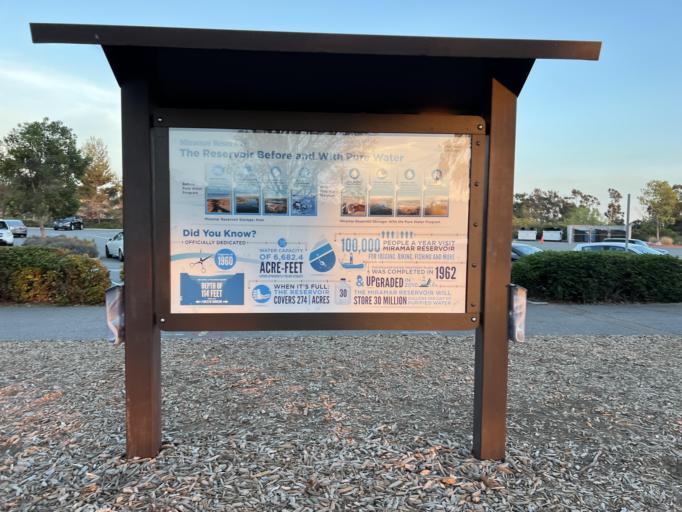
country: US
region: California
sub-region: San Diego County
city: Poway
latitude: 32.9140
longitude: -117.0990
